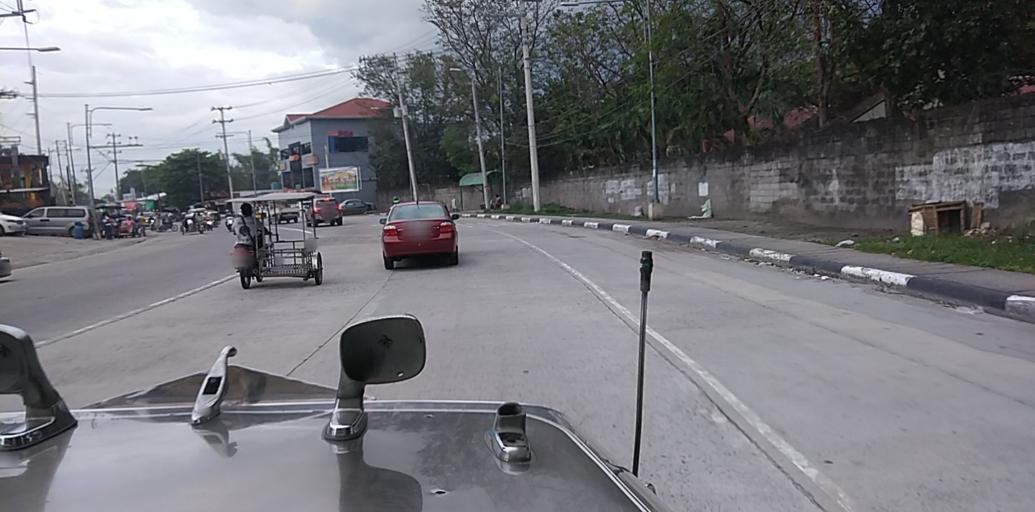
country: PH
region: Central Luzon
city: Santol
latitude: 15.1531
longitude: 120.5601
